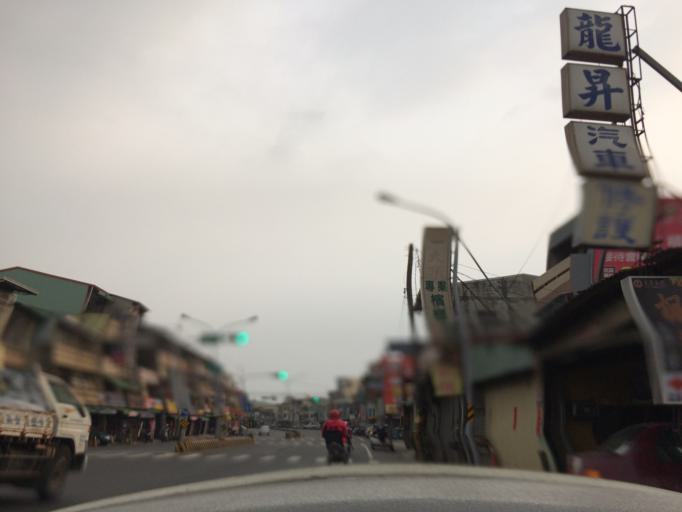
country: TW
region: Taiwan
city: Zhongxing New Village
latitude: 24.0436
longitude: 120.6919
